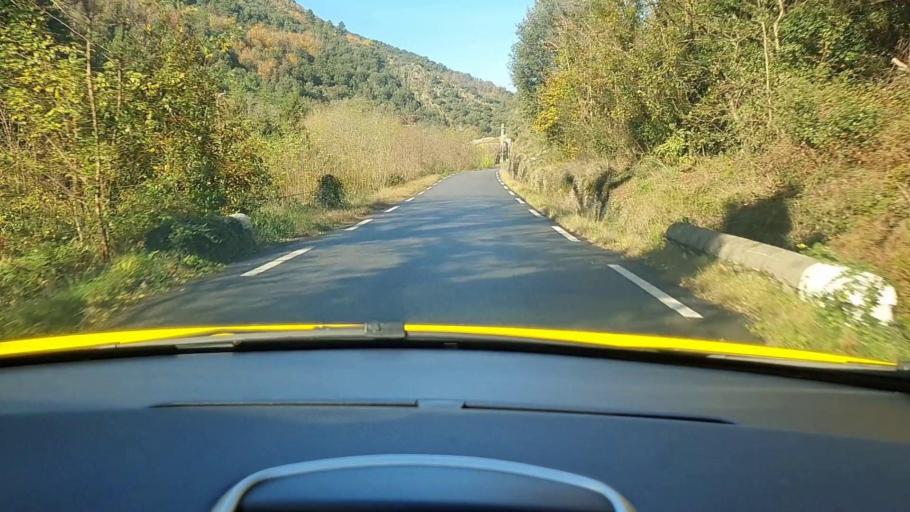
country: FR
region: Languedoc-Roussillon
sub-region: Departement du Gard
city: Valleraugue
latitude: 44.1312
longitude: 3.7580
